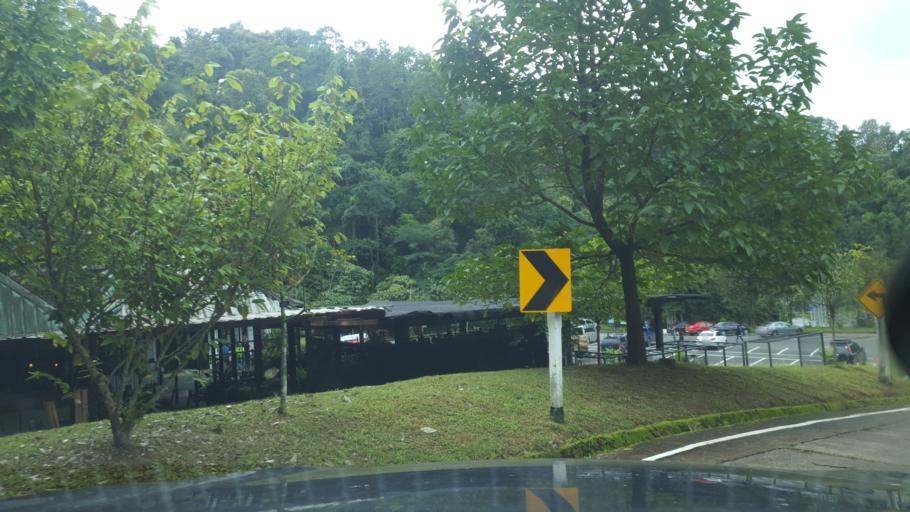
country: TH
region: Chiang Mai
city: Samoeng
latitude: 18.8869
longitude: 98.8633
